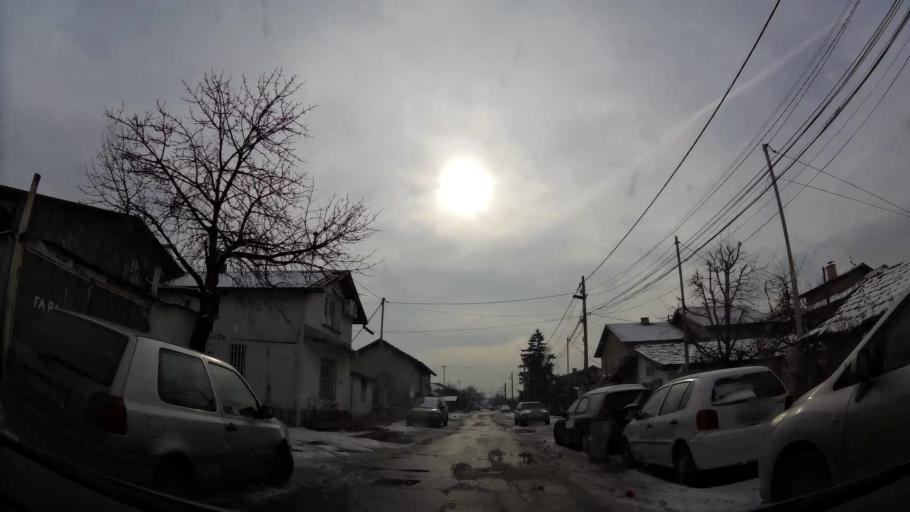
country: BG
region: Sofia-Capital
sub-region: Stolichna Obshtina
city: Sofia
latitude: 42.7094
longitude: 23.4043
